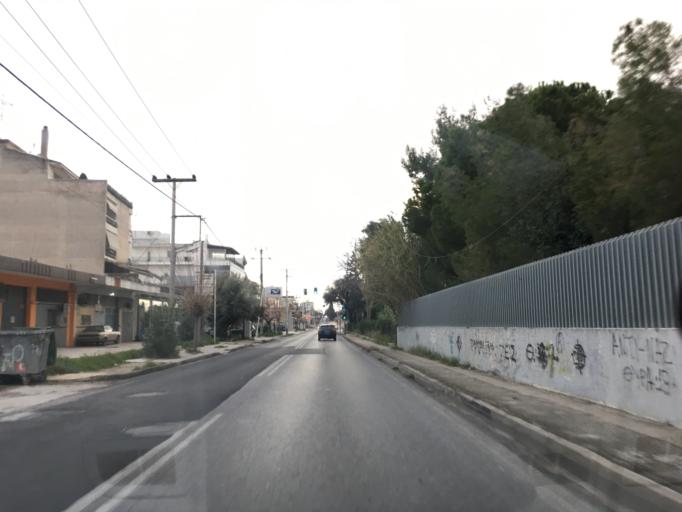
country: GR
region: Attica
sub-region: Nomarchia Athinas
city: Nea Filadelfeia
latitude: 38.0449
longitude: 23.7282
